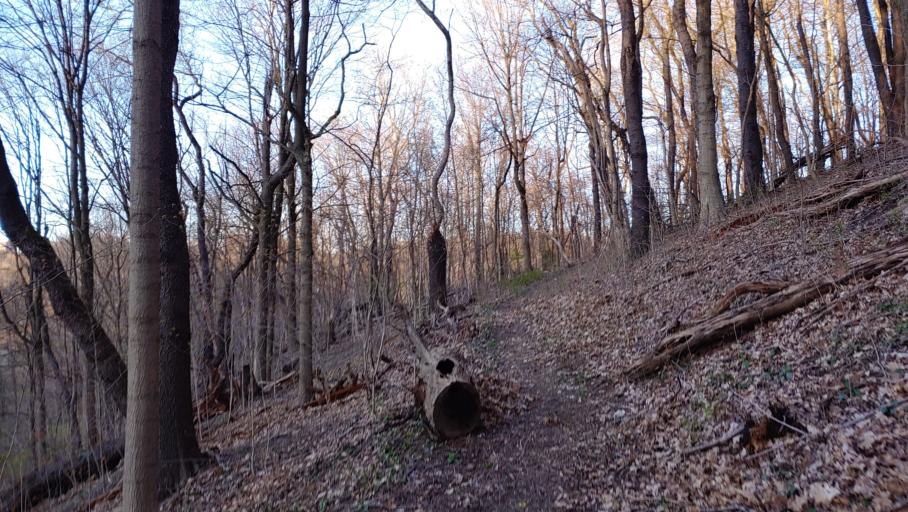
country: US
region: Pennsylvania
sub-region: Allegheny County
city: Green Tree
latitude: 40.4276
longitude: -80.0280
